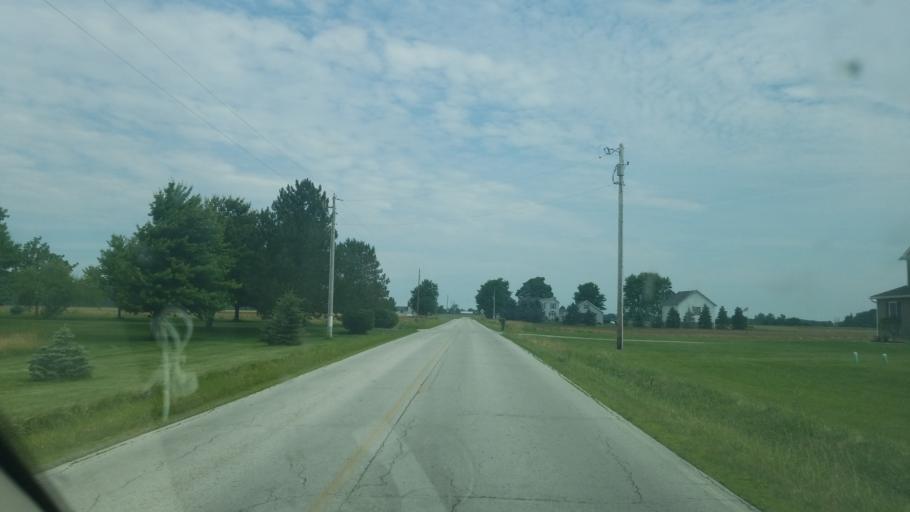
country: US
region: Ohio
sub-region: Seneca County
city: Fostoria
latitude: 41.0712
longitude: -83.4774
